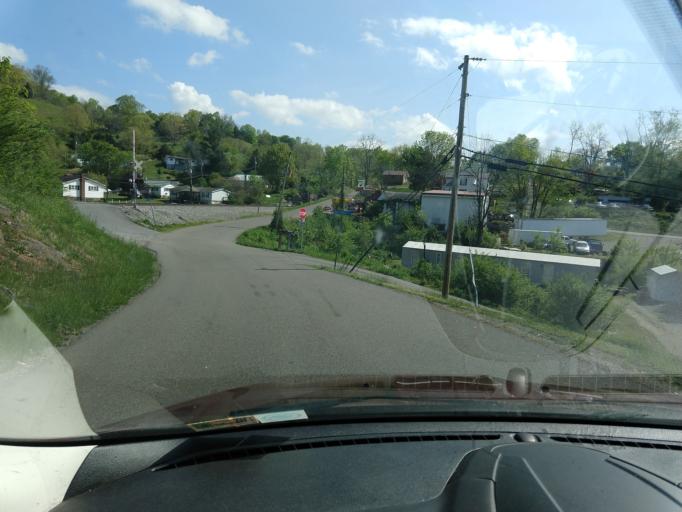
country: US
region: Virginia
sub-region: Russell County
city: Honaker
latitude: 37.0186
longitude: -81.9729
